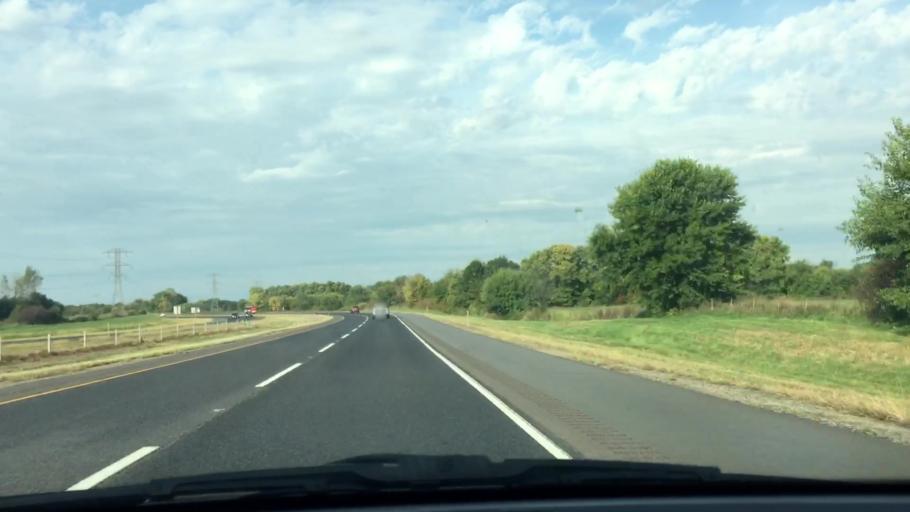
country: US
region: Illinois
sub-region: Whiteside County
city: Rock Falls
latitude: 41.7665
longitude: -89.6207
